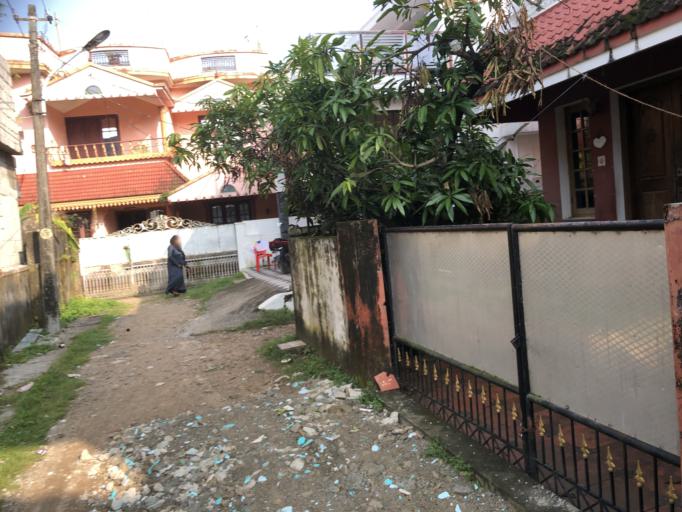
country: IN
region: Kerala
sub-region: Ernakulam
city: Cochin
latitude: 9.9628
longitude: 76.2499
